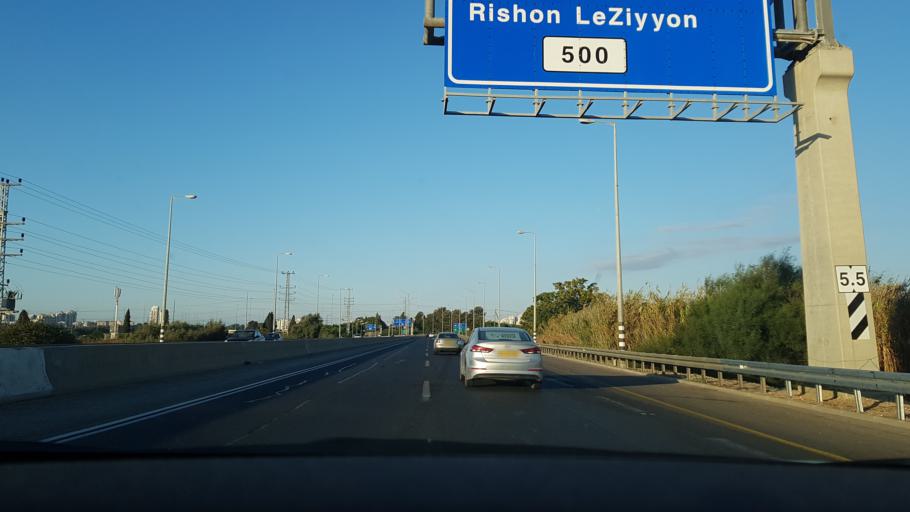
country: IL
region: Central District
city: Ness Ziona
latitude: 31.9445
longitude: 34.7815
